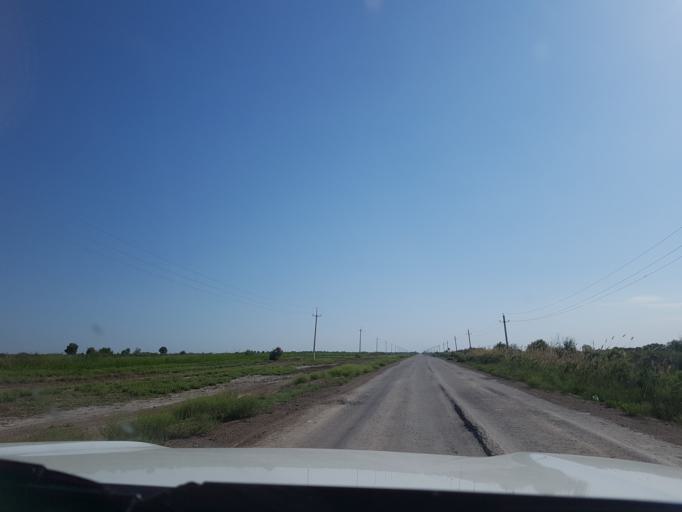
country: TM
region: Dasoguz
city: Koeneuergench
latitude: 42.0773
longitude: 58.8692
